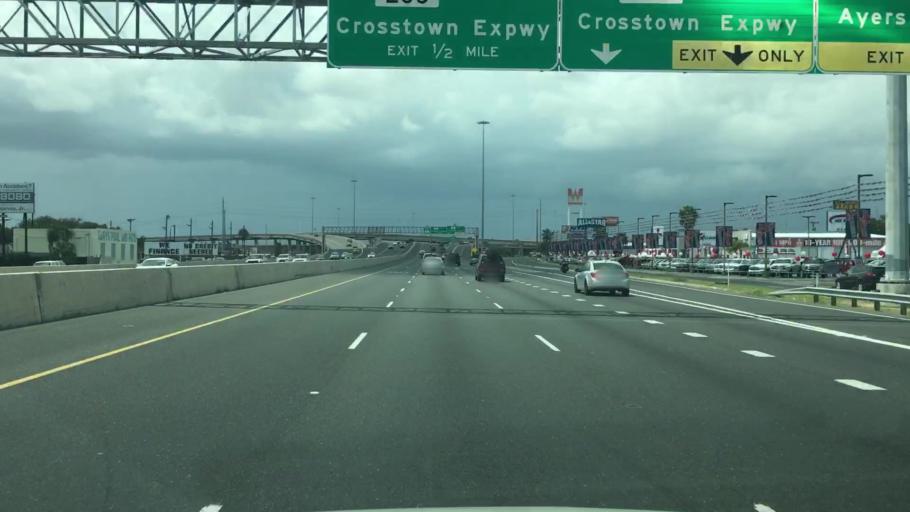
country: US
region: Texas
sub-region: Nueces County
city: Corpus Christi
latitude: 27.7337
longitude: -97.4233
